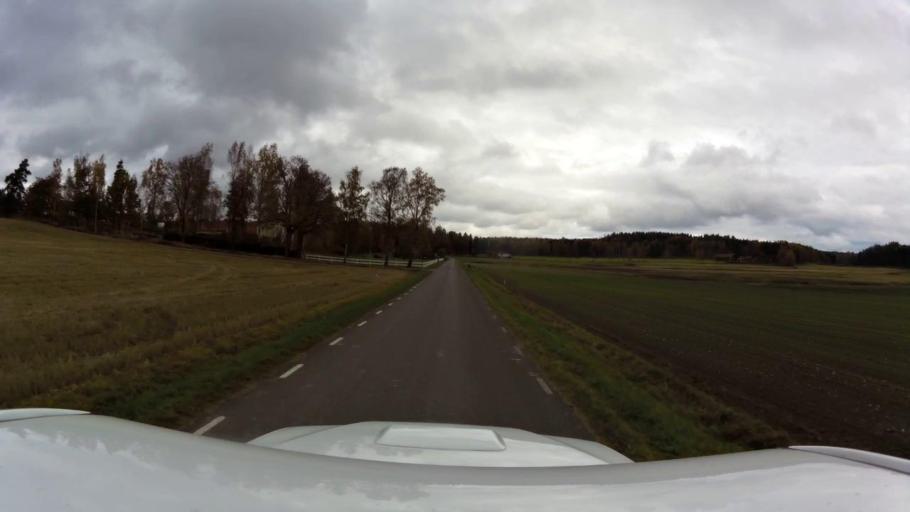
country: SE
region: OEstergoetland
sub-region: Motala Kommun
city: Borensberg
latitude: 58.5710
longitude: 15.3893
